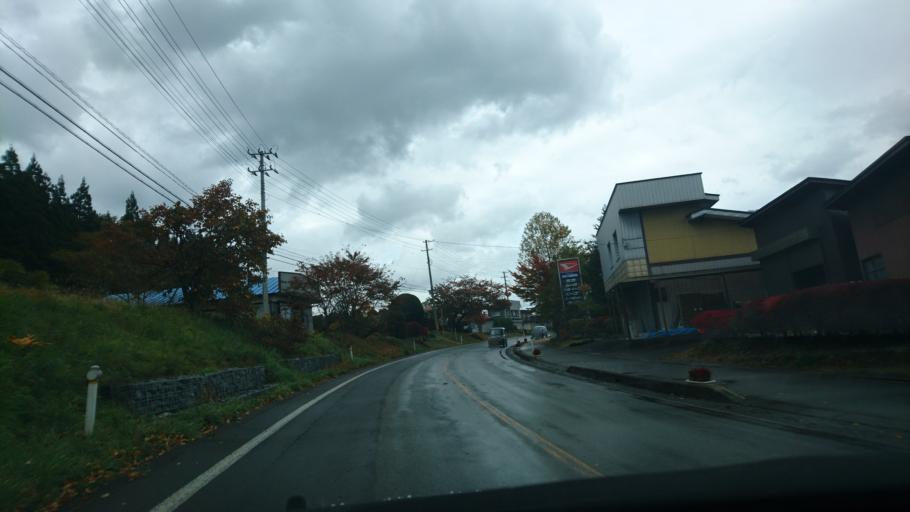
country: JP
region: Iwate
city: Shizukuishi
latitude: 39.6714
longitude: 140.9831
